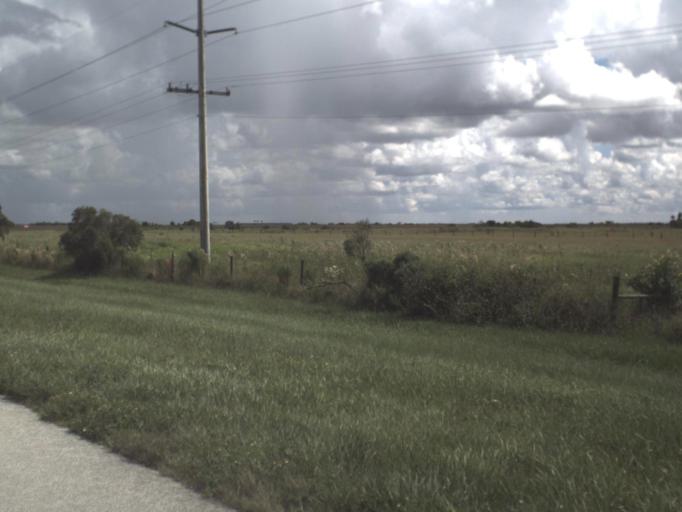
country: US
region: Florida
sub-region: Highlands County
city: Placid Lakes
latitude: 27.2096
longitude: -81.5954
